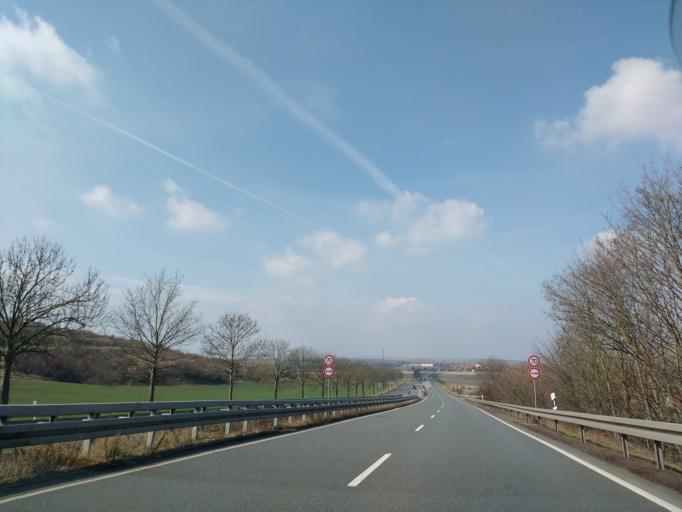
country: DE
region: Saxony-Anhalt
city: Roblingen am See
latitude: 51.4861
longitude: 11.6923
